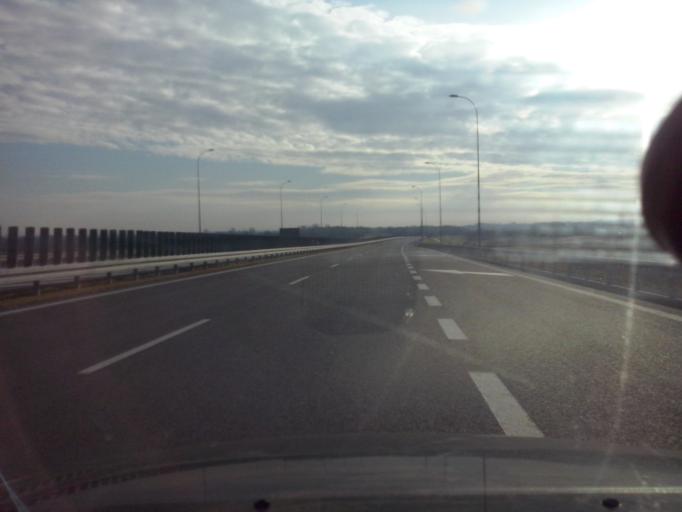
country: PL
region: Subcarpathian Voivodeship
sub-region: Powiat rzeszowski
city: Rudna Wielka
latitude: 50.1007
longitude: 21.9300
